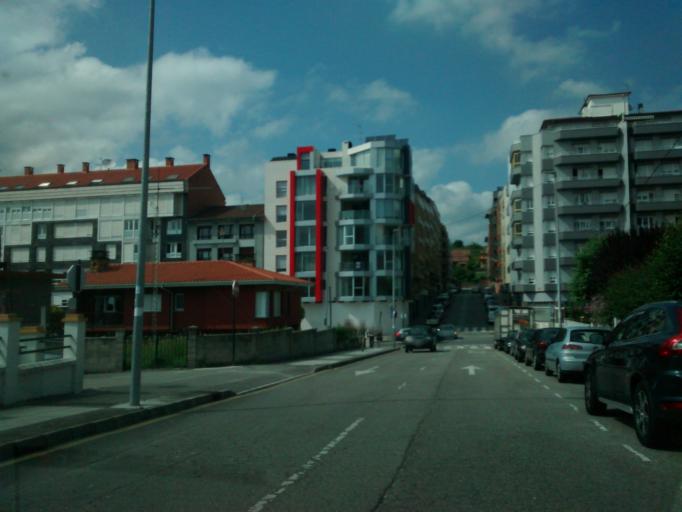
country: ES
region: Asturias
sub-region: Province of Asturias
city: Pola de Siero
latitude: 43.3922
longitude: -5.6573
